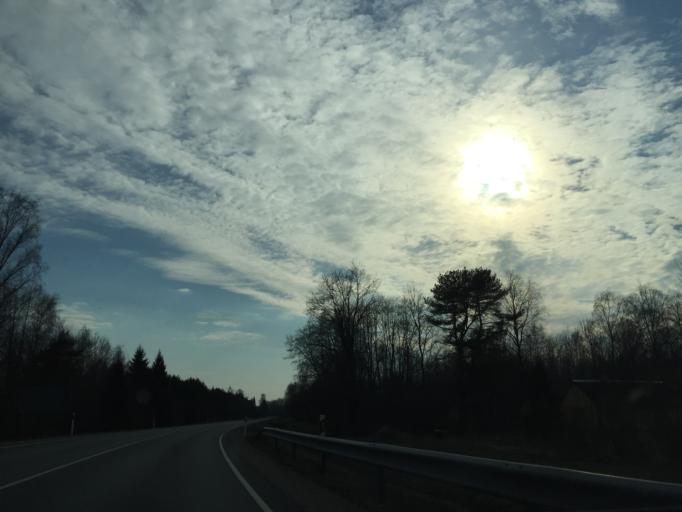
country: EE
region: Jogevamaa
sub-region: Mustvee linn
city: Mustvee
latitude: 58.9390
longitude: 27.0433
